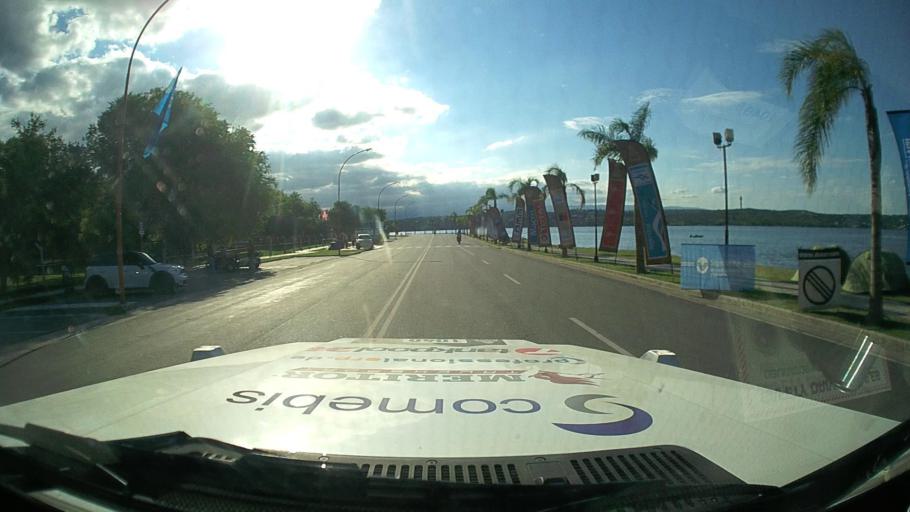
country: AR
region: Cordoba
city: Villa Carlos Paz
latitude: -31.3956
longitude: -64.4735
